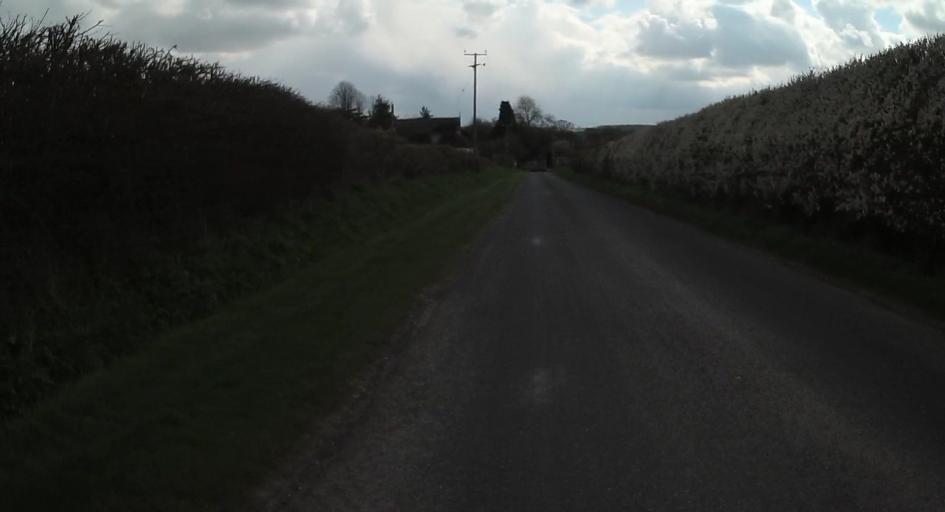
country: GB
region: England
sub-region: Hampshire
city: Kings Worthy
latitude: 51.0901
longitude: -1.2031
